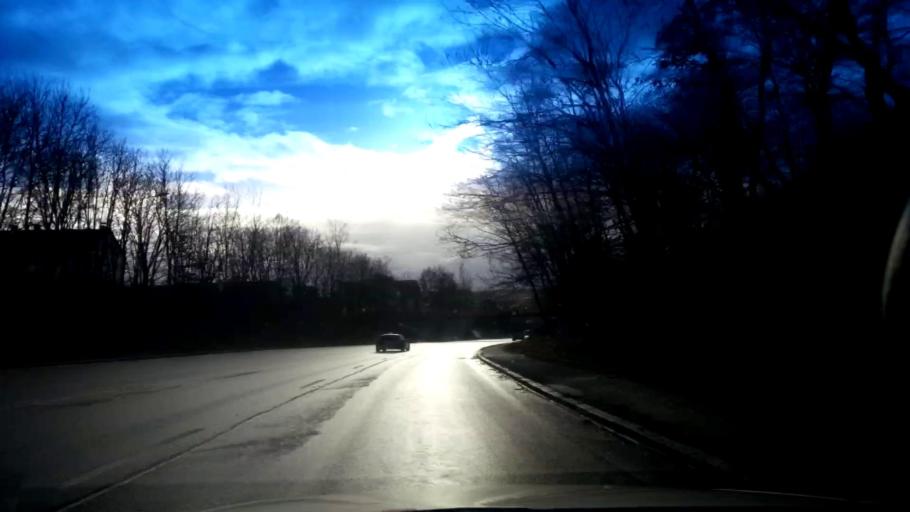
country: CZ
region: Karlovarsky
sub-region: Okres Cheb
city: Cheb
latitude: 50.0887
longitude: 12.3710
